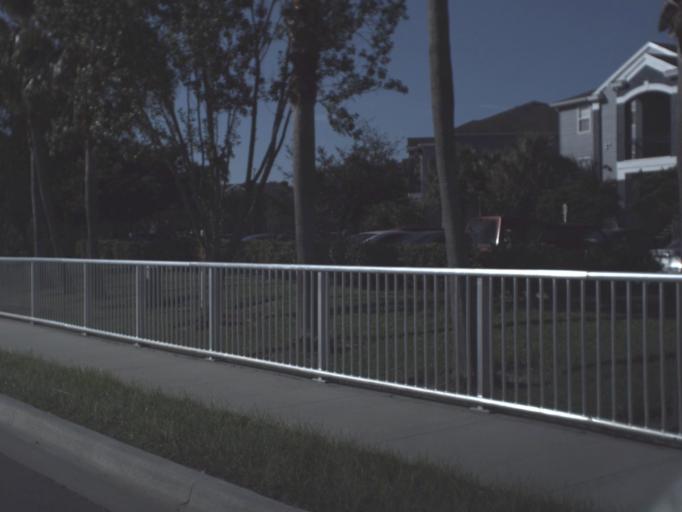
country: US
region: Florida
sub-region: Lee County
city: Fort Myers
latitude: 26.6093
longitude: -81.8516
